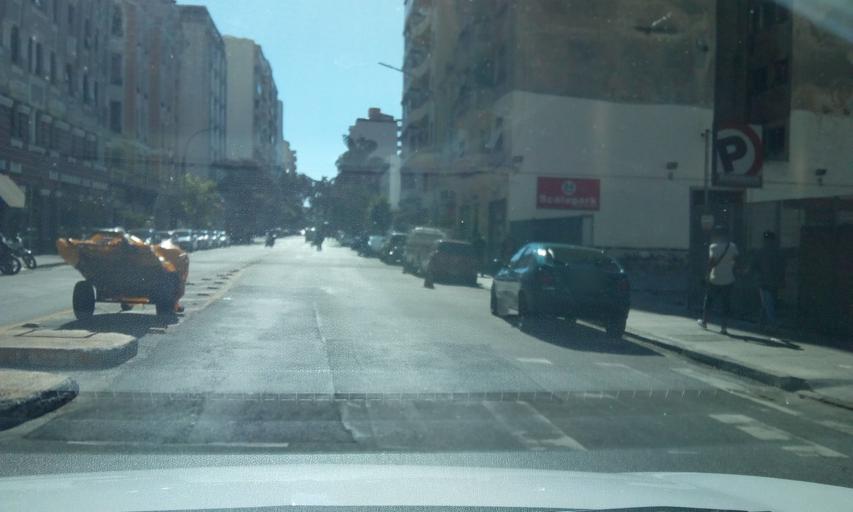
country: BR
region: Sao Paulo
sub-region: Sao Paulo
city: Sao Paulo
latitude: -23.5397
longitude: -46.6433
